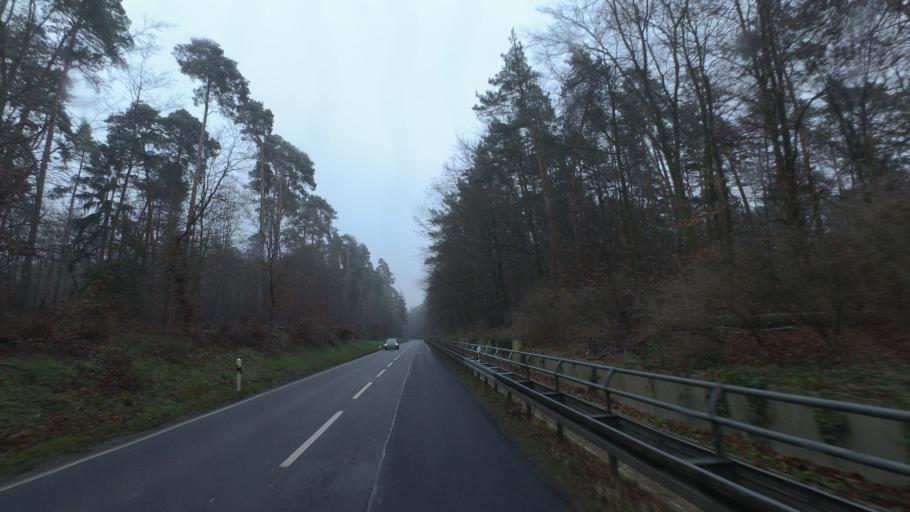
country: DE
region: Hesse
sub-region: Regierungsbezirk Darmstadt
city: Rodgau
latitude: 50.0697
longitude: 8.9196
